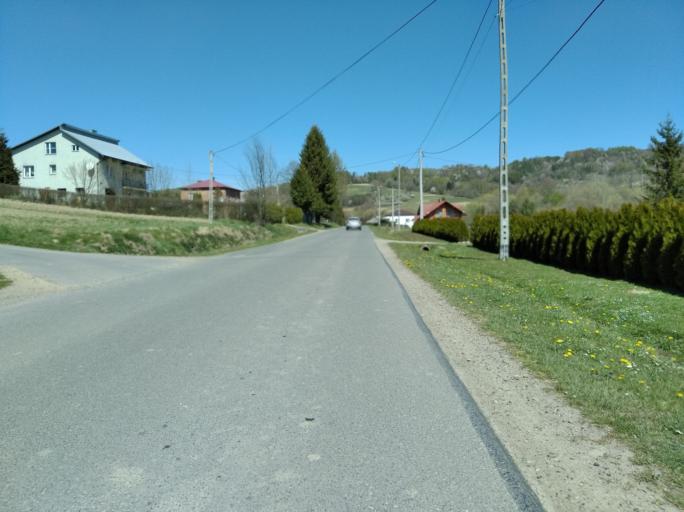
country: PL
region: Subcarpathian Voivodeship
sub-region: Powiat brzozowski
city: Dydnia
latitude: 49.6974
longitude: 22.1518
